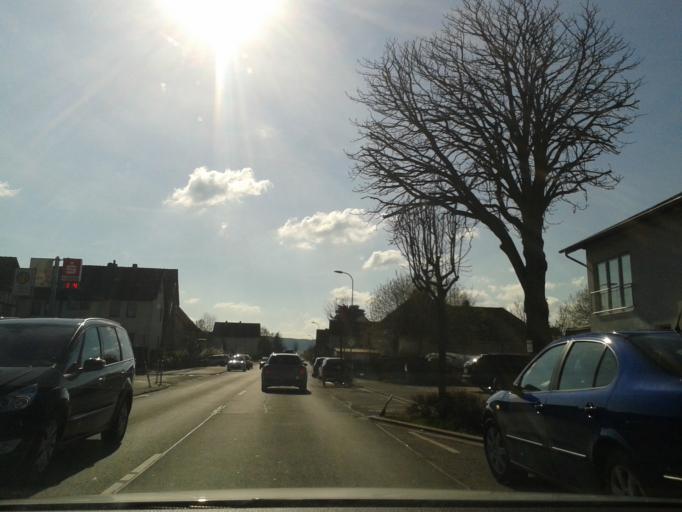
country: DE
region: Hesse
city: Wetter
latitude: 50.8612
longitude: 8.7025
